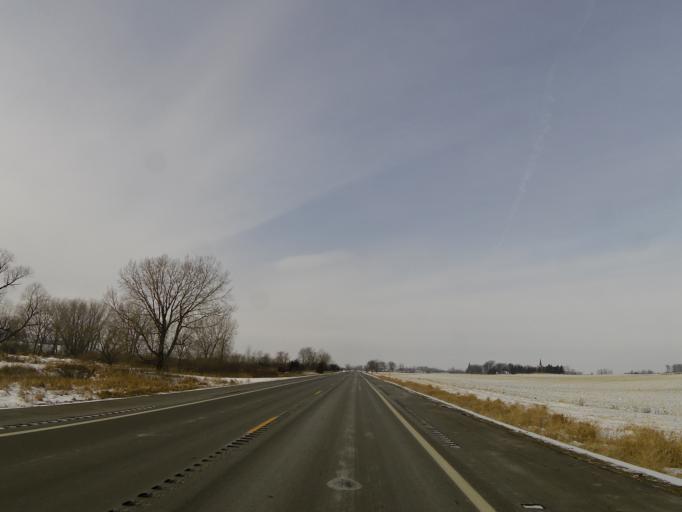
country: US
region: Minnesota
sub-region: McLeod County
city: Hutchinson
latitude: 44.9137
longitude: -94.4544
